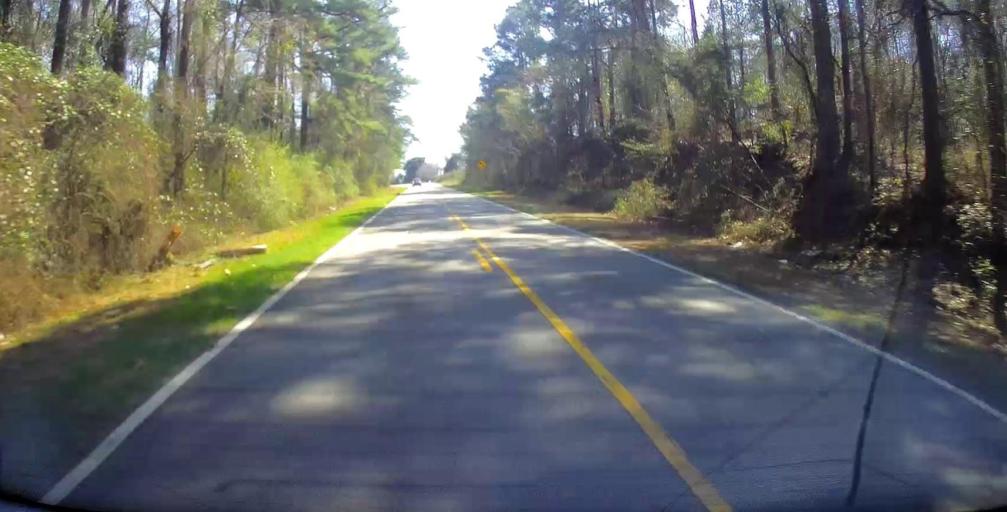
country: US
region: Georgia
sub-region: Peach County
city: Byron
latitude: 32.5802
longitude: -83.7572
